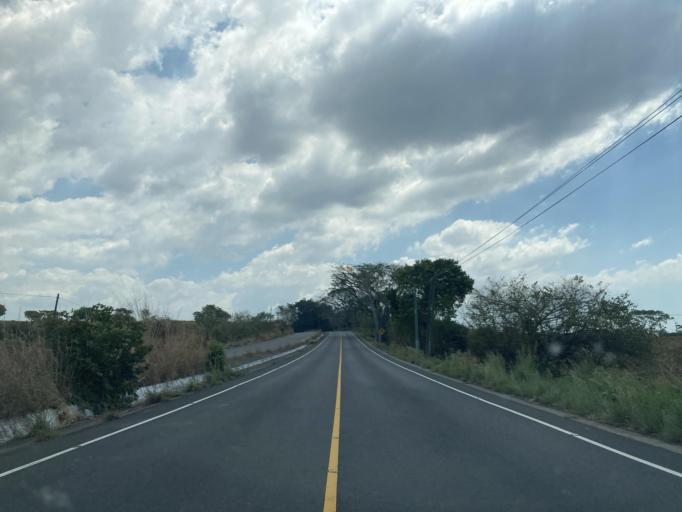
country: GT
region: Santa Rosa
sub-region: Municipio de Taxisco
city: Taxisco
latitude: 14.0928
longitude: -90.5207
